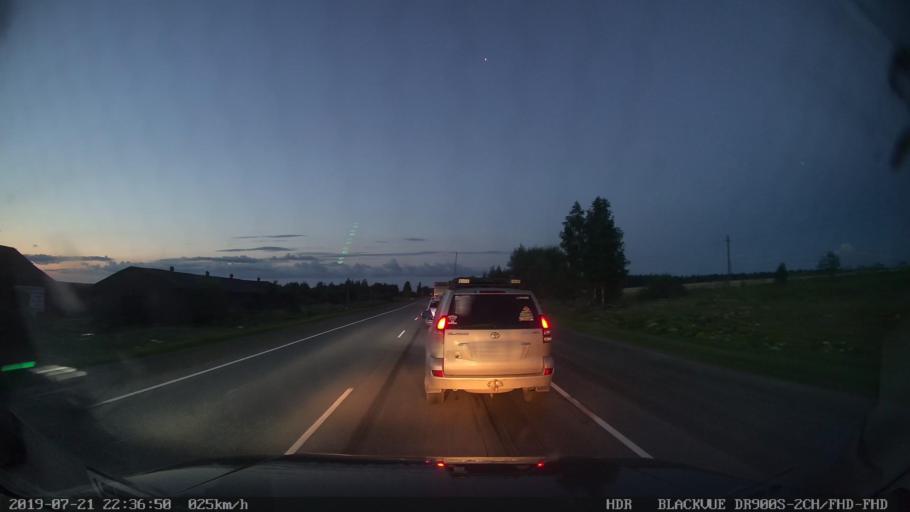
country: RU
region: Perm
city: Chaykovskaya
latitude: 58.0455
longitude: 55.5829
